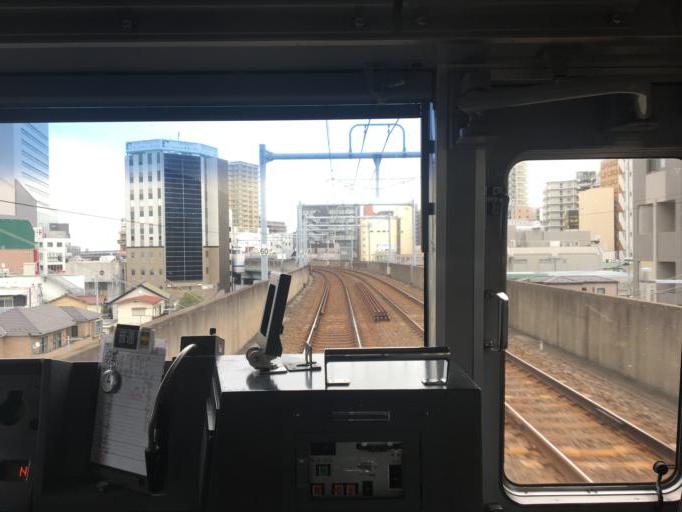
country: JP
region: Chiba
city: Funabashi
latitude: 35.7004
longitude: 139.9826
